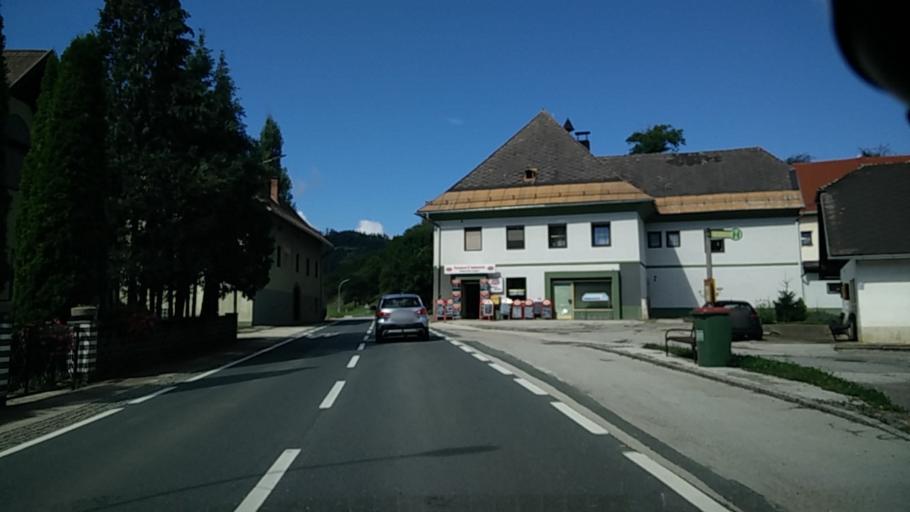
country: AT
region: Carinthia
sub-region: Politischer Bezirk Sankt Veit an der Glan
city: Bruckl
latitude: 46.7489
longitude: 14.5259
